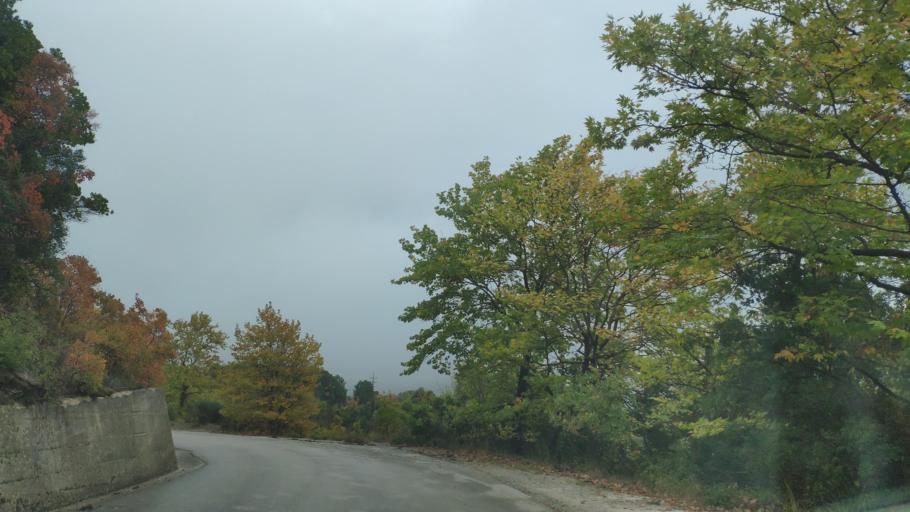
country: GR
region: Epirus
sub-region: Nomos Thesprotias
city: Paramythia
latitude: 39.4728
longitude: 20.6690
